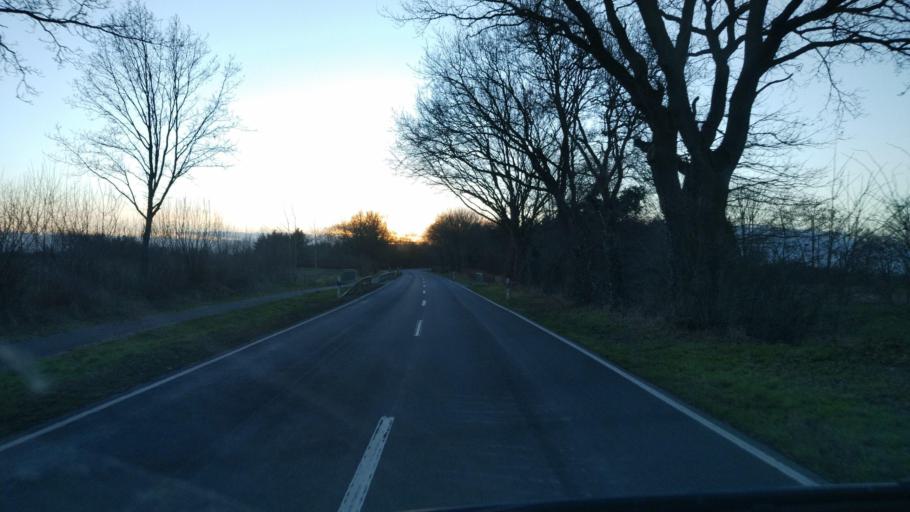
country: DE
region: Schleswig-Holstein
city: Dorpstedt
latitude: 54.4464
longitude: 9.3889
